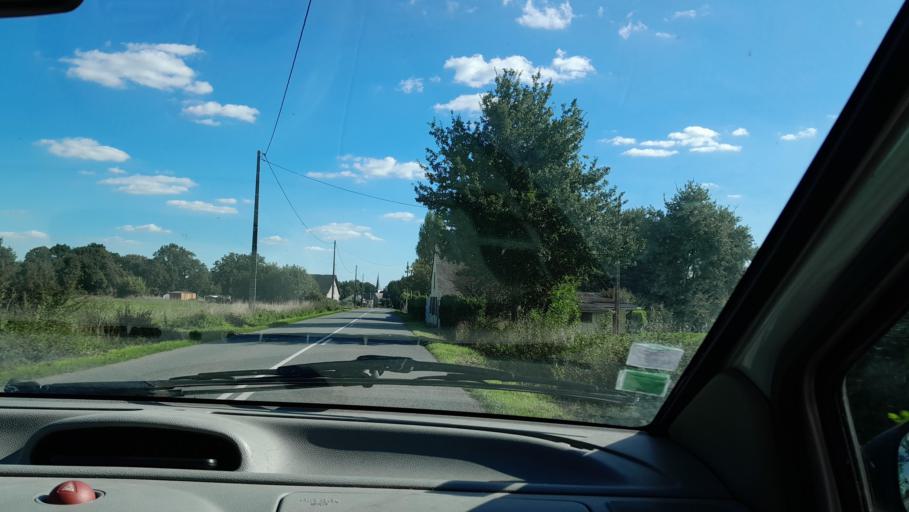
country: FR
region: Pays de la Loire
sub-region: Departement de la Mayenne
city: Ballots
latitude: 47.9561
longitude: -1.1082
